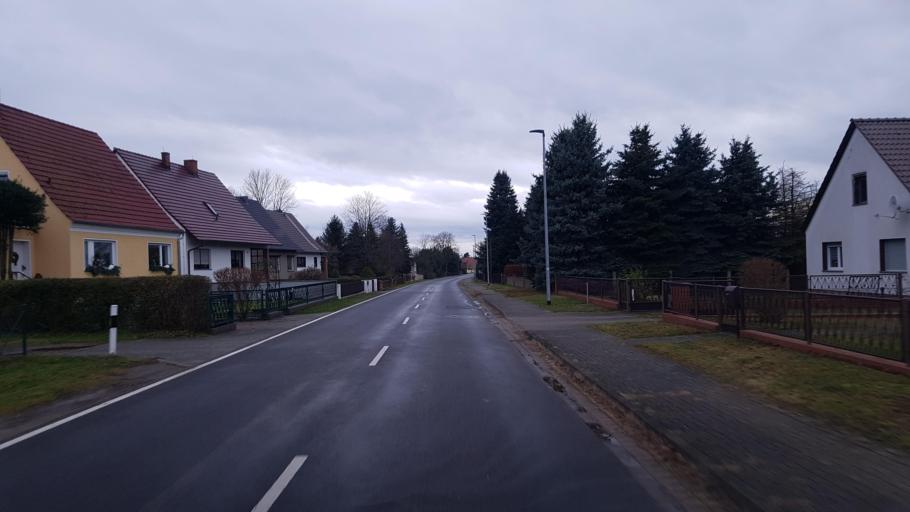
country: DE
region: Brandenburg
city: Schlepzig
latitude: 52.0534
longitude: 14.0071
